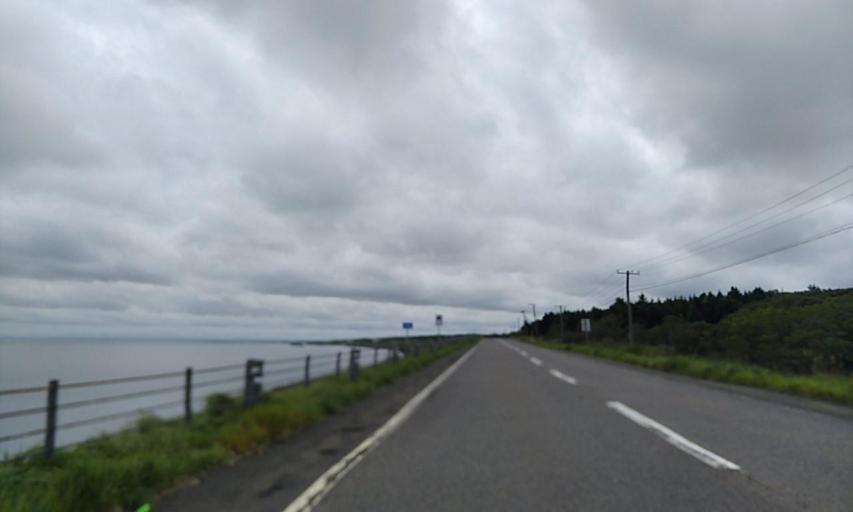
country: JP
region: Hokkaido
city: Shibetsu
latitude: 43.4418
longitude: 145.2620
